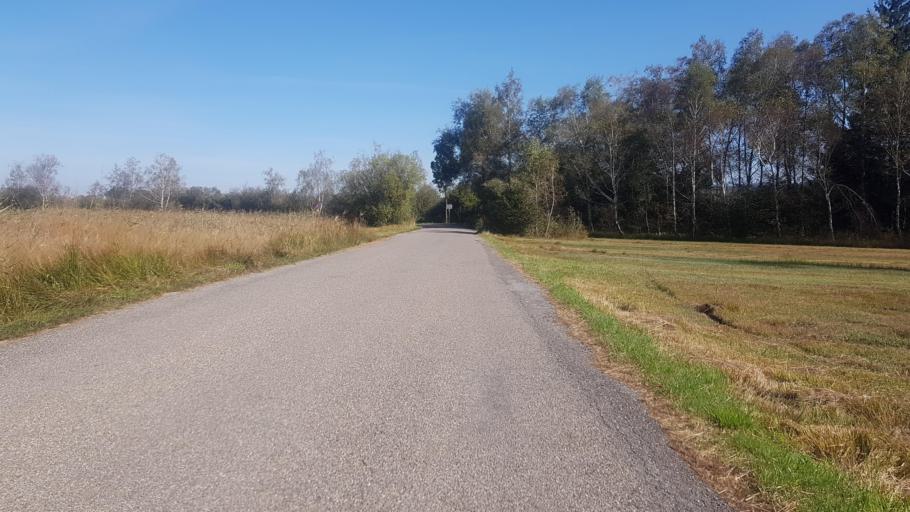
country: AT
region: Vorarlberg
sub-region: Politischer Bezirk Bregenz
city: Hochst
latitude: 47.4916
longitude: 9.6264
